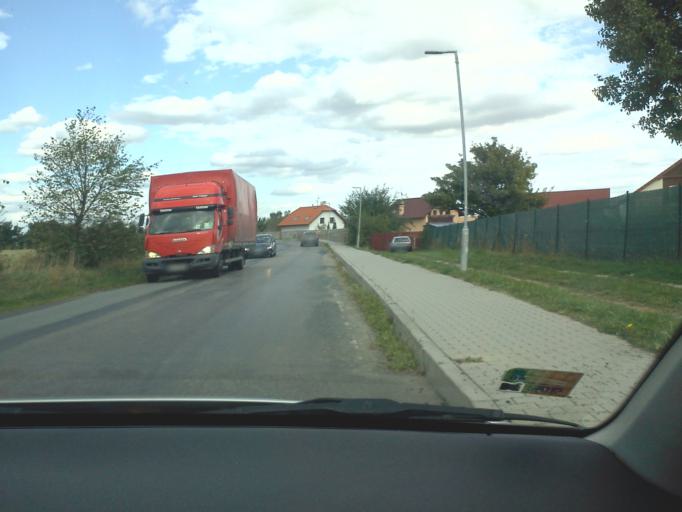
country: CZ
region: Central Bohemia
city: Mukarov
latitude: 50.0185
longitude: 14.7868
